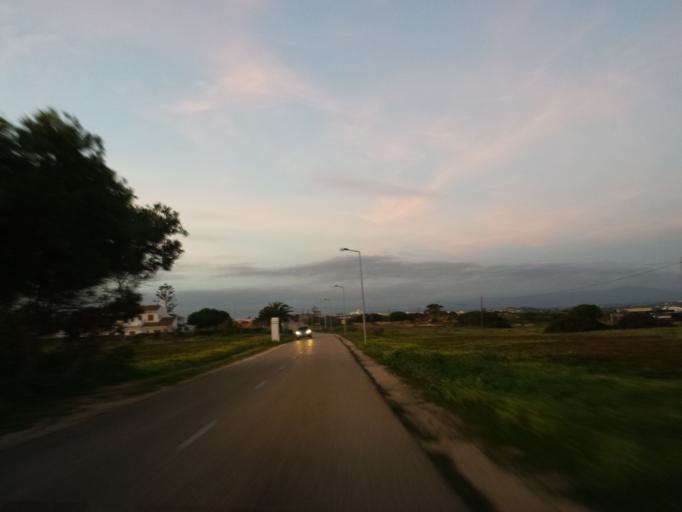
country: PT
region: Faro
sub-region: Lagos
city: Lagos
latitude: 37.0848
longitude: -8.6707
